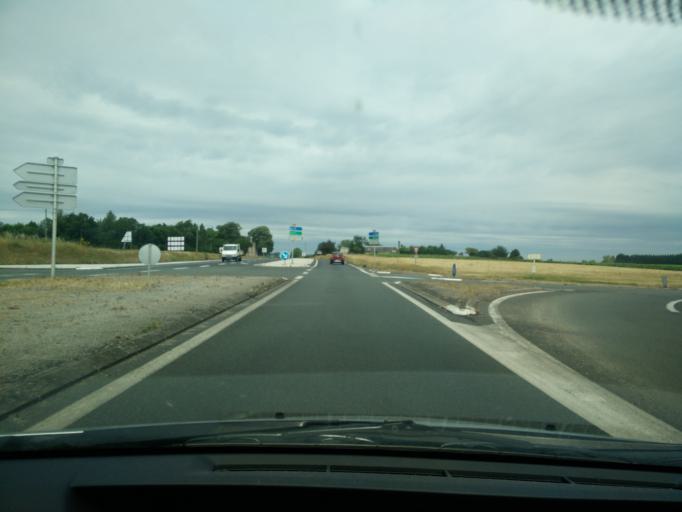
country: FR
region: Pays de la Loire
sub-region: Departement de Maine-et-Loire
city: Brissac-Quince
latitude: 47.3635
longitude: -0.4494
